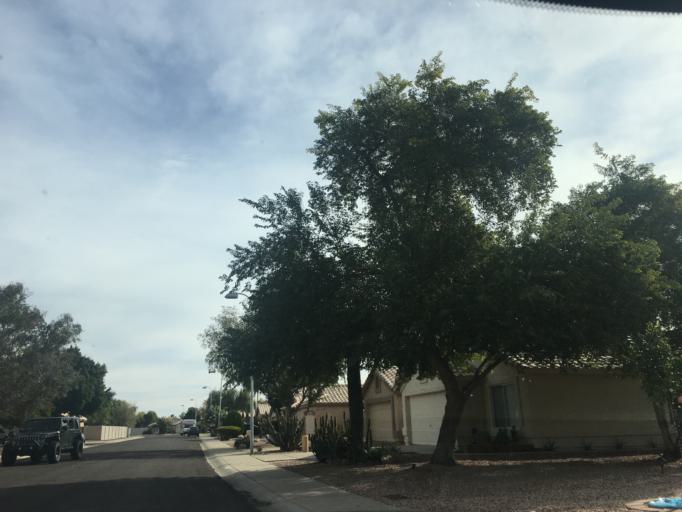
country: US
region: Arizona
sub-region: Maricopa County
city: Gilbert
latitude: 33.3492
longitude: -111.8096
